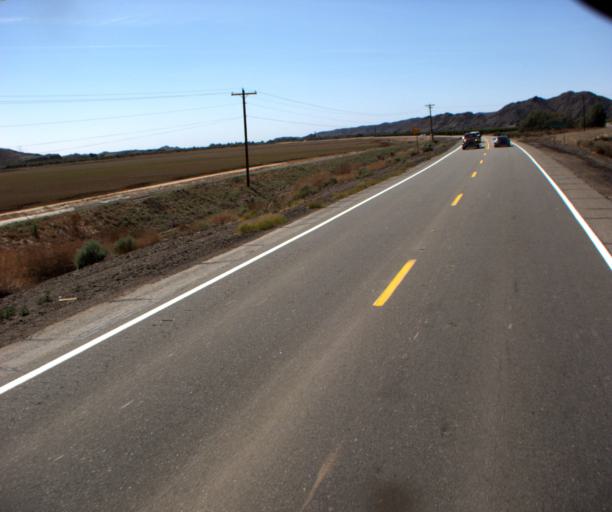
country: US
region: Arizona
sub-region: Yuma County
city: Fortuna Foothills
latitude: 32.7689
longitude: -114.3978
